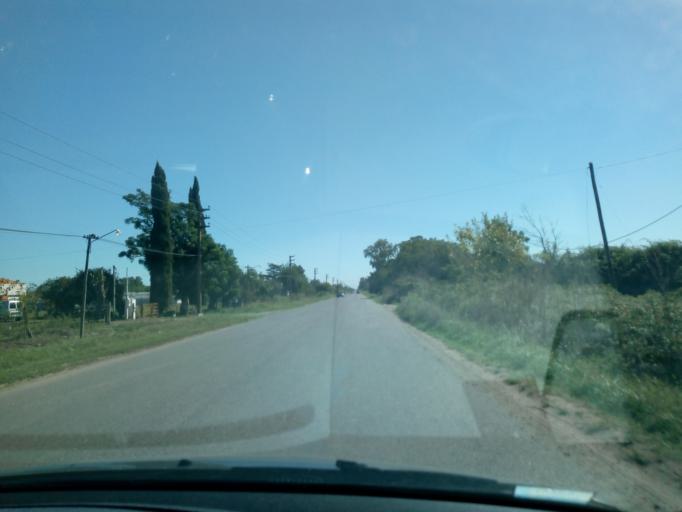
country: AR
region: Buenos Aires
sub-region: Partido de La Plata
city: La Plata
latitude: -35.0096
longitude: -58.0292
